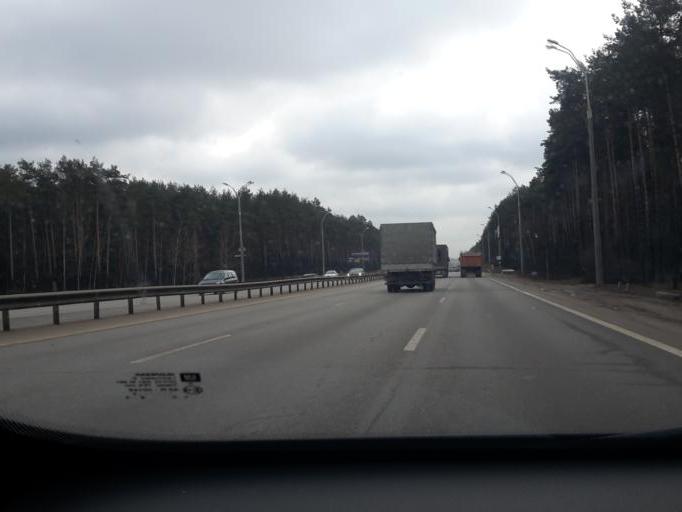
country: BY
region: Minsk
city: Borovlyany
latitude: 53.9556
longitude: 27.6386
